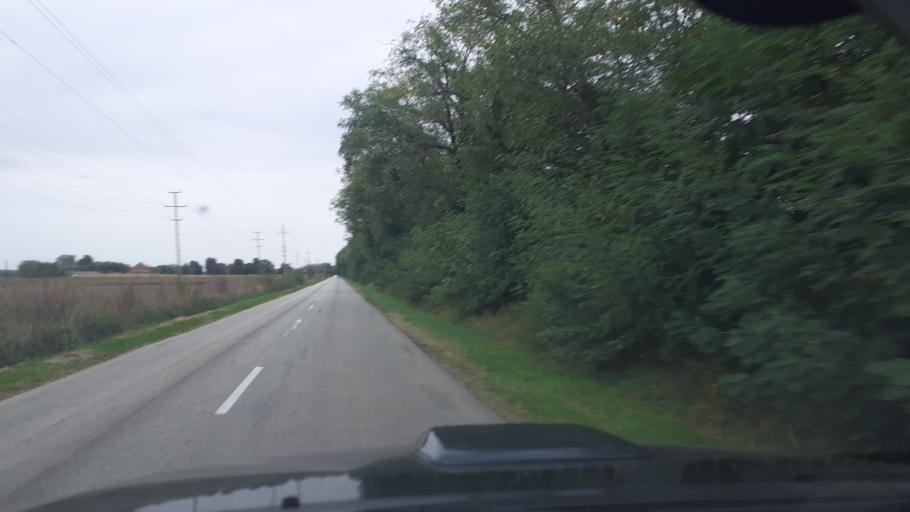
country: HU
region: Tolna
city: Dunafoldvar
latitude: 46.8377
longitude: 18.8967
